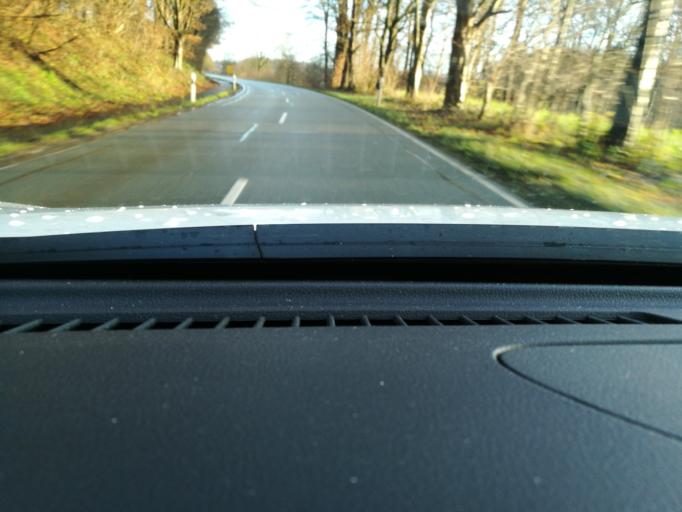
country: DE
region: Schleswig-Holstein
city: Ascheffel
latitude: 54.4105
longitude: 9.6956
